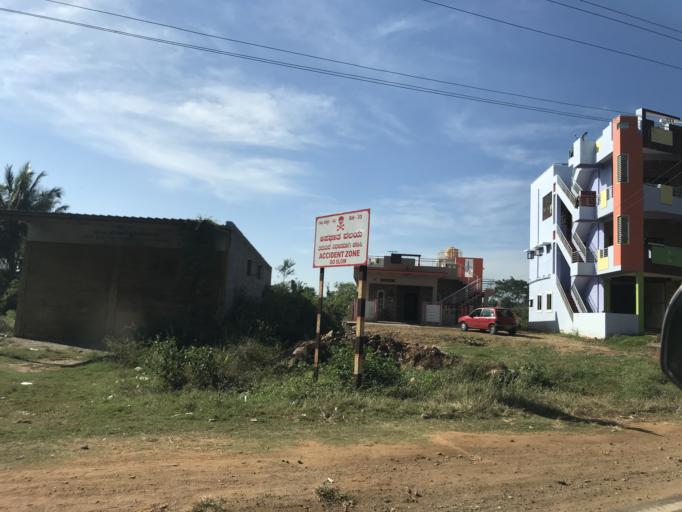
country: IN
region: Karnataka
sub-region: Mysore
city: Mysore
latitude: 12.2272
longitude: 76.5834
